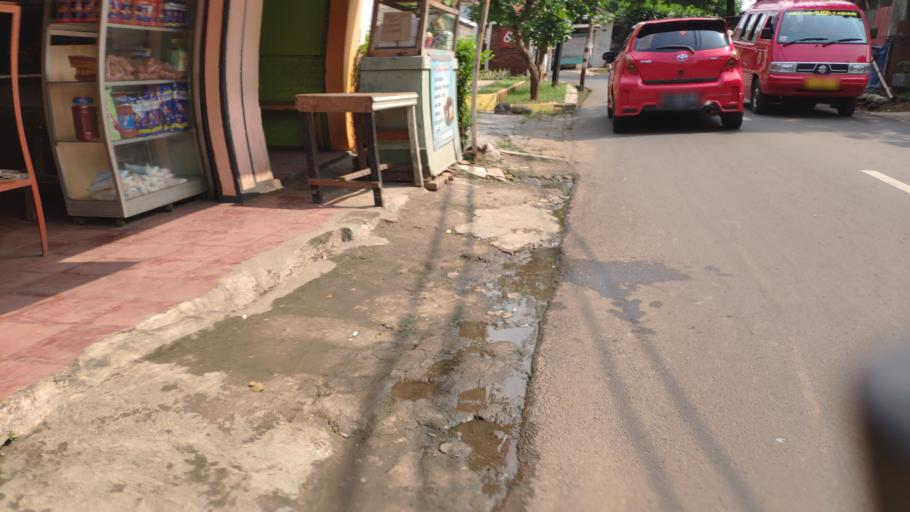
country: ID
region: West Java
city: Depok
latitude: -6.3198
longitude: 106.8187
